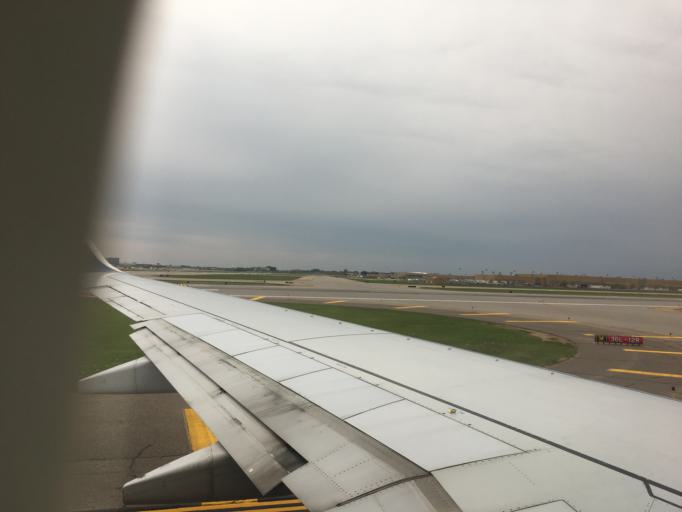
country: US
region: Minnesota
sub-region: Hennepin County
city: Richfield
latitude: 44.8845
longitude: -93.2232
